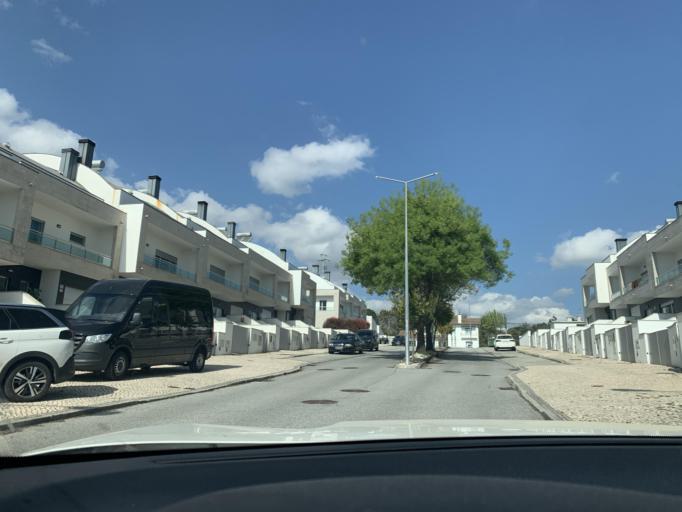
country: PT
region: Viseu
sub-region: Viseu
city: Rio de Loba
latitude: 40.6521
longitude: -7.8796
